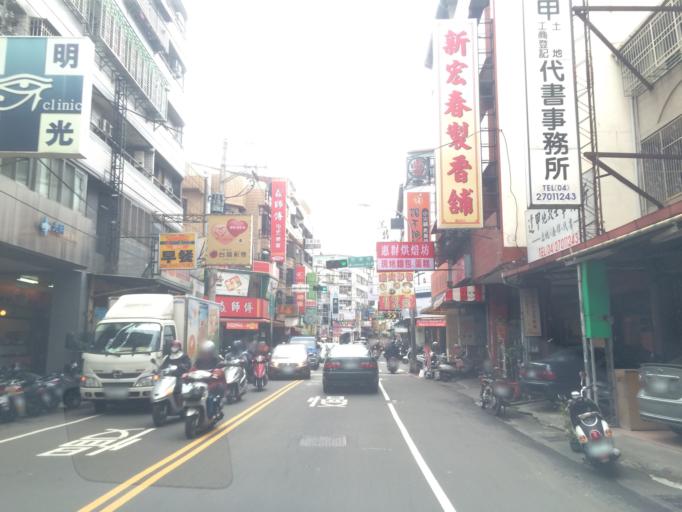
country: TW
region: Taiwan
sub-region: Taichung City
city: Taichung
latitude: 24.1784
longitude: 120.6413
